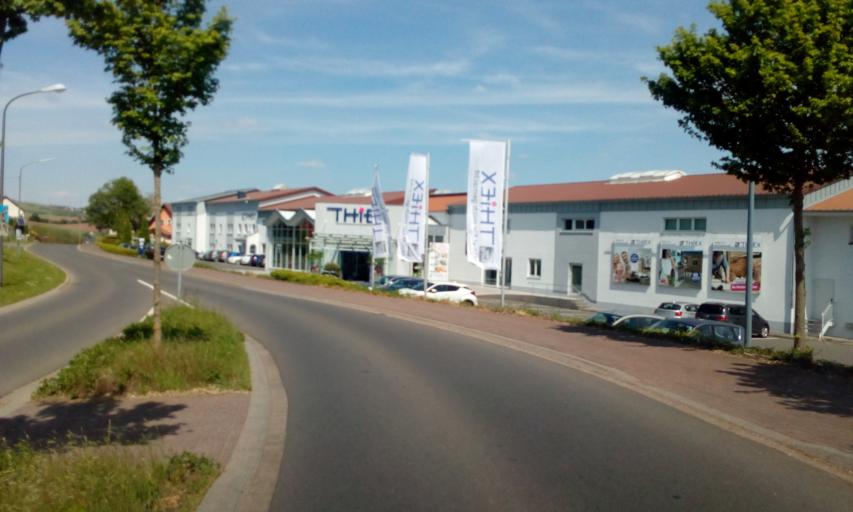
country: DE
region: Rheinland-Pfalz
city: Geichlingen
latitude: 49.9496
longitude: 6.2651
